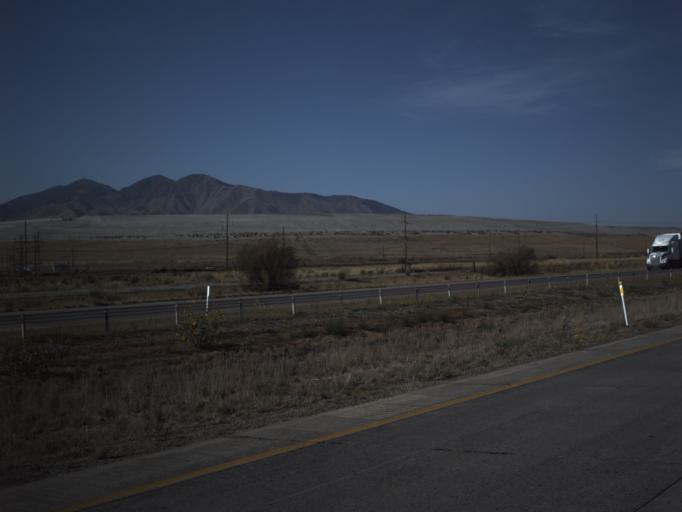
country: US
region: Utah
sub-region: Salt Lake County
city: Magna
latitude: 40.7711
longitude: -112.0901
